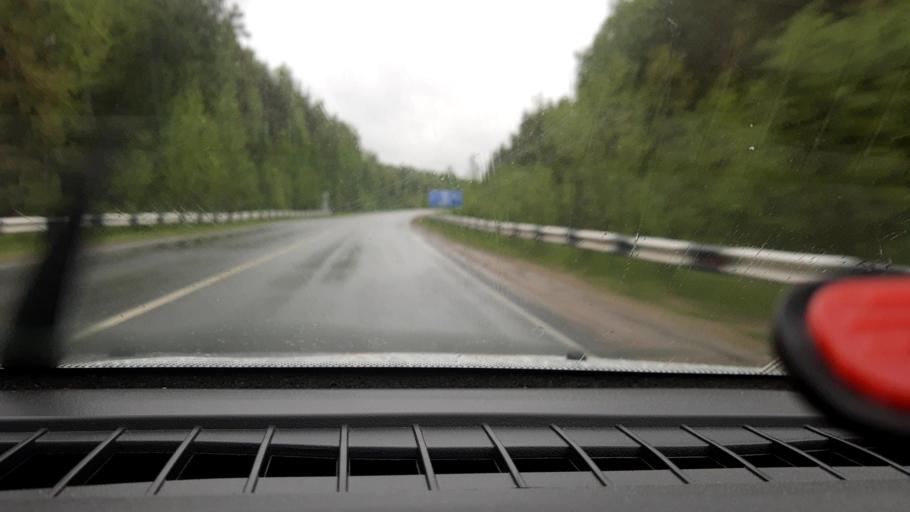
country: RU
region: Nizjnij Novgorod
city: Semenov
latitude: 56.8036
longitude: 44.4614
